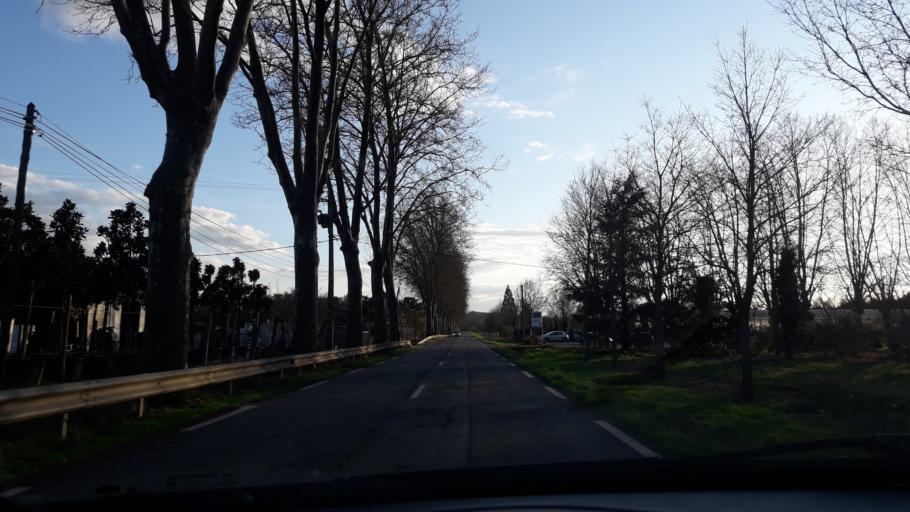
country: FR
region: Midi-Pyrenees
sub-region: Departement de la Haute-Garonne
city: Montaigut-sur-Save
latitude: 43.7029
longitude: 1.2408
